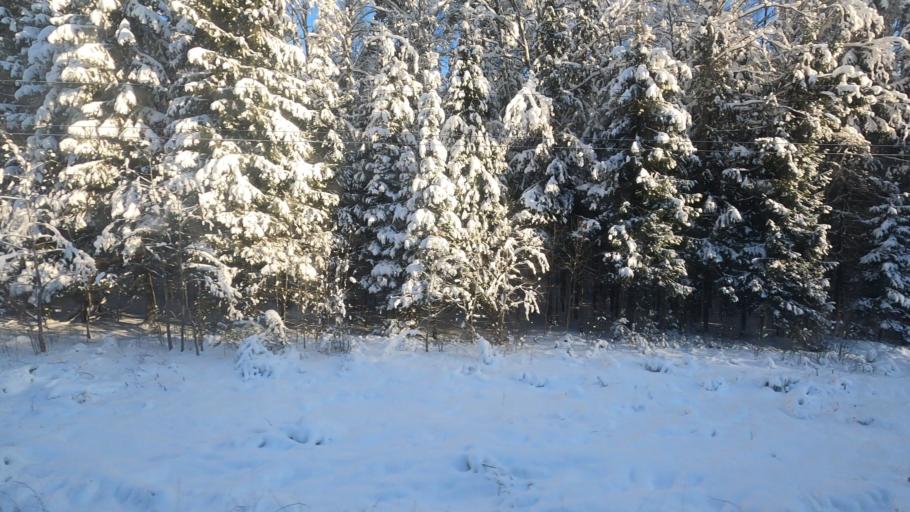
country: RU
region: Moskovskaya
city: Novo-Nikol'skoye
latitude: 56.6338
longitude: 37.5627
